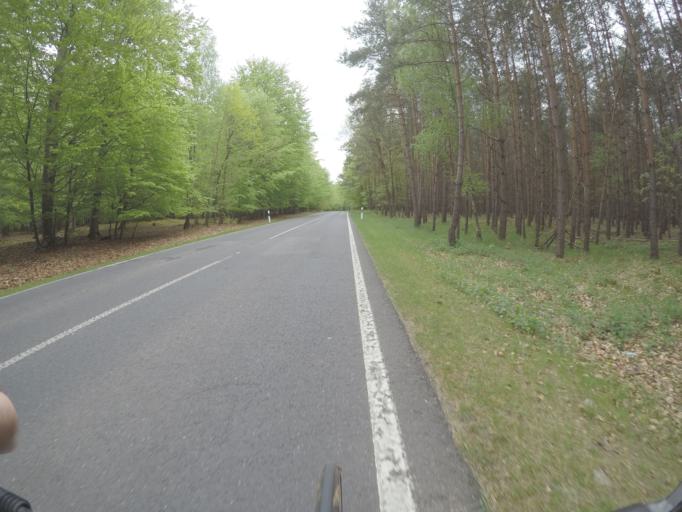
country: DE
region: Brandenburg
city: Joachimsthal
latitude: 52.9552
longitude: 13.7535
